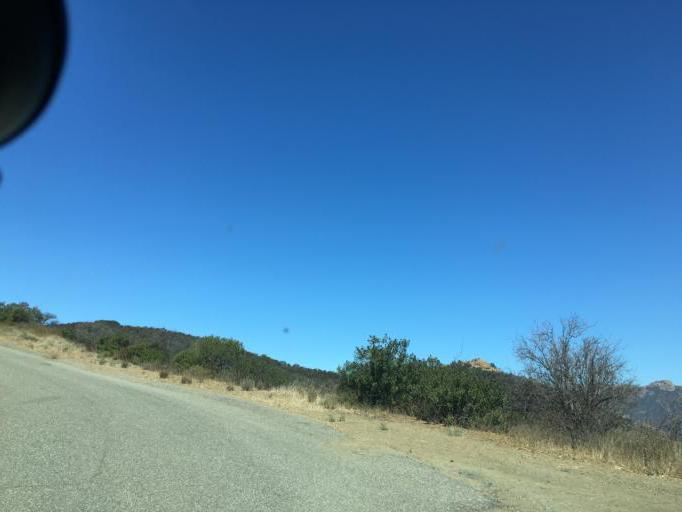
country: US
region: California
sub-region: Los Angeles County
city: Malibu
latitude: 34.0743
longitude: -118.9021
